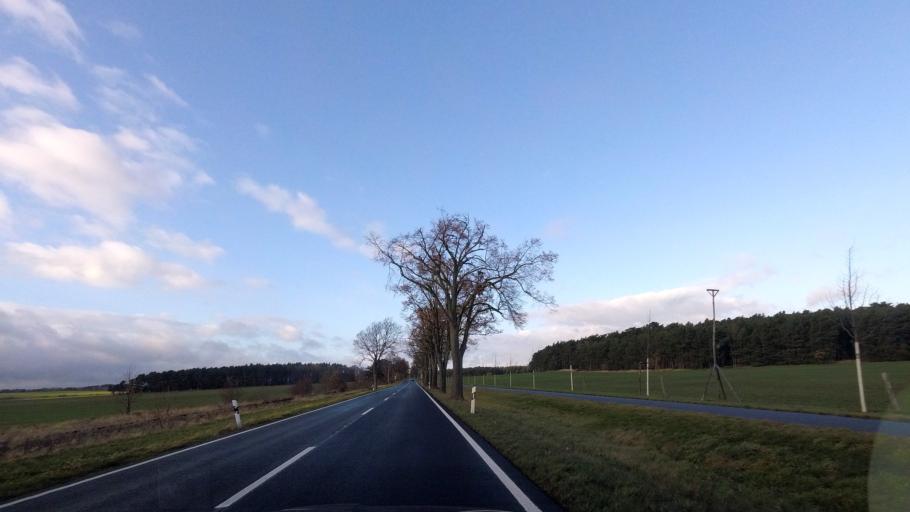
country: DE
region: Brandenburg
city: Belzig
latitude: 52.1181
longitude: 12.6432
